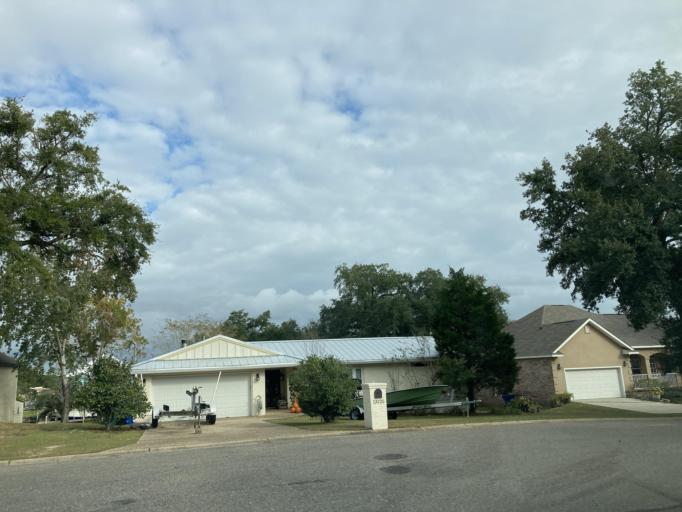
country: US
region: Mississippi
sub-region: Jackson County
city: Ocean Springs
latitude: 30.4264
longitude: -88.8276
